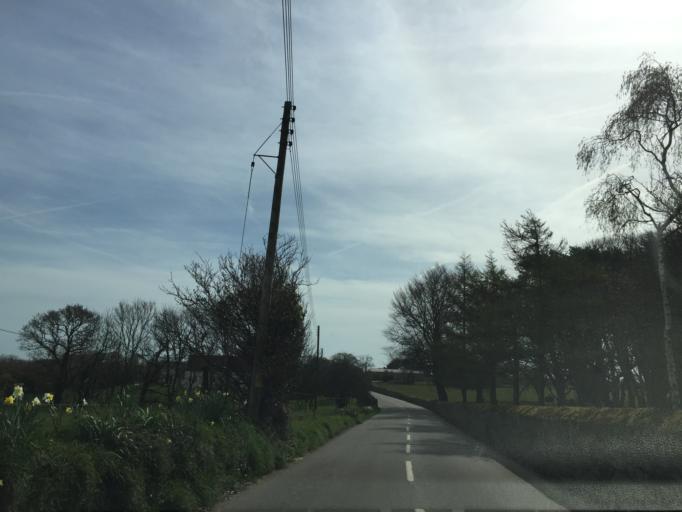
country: JE
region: St Helier
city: Saint Helier
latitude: 49.2293
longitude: -2.0420
